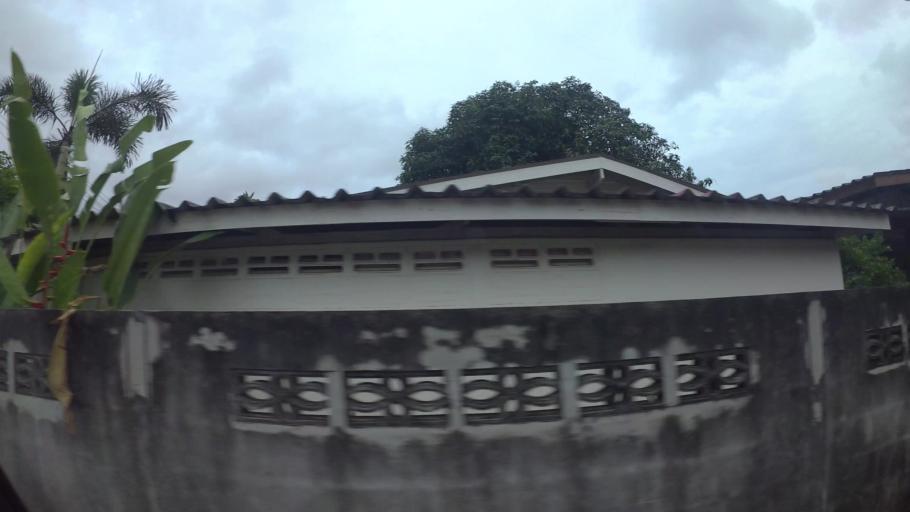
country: TH
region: Rayong
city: Rayong
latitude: 12.6784
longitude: 101.2635
